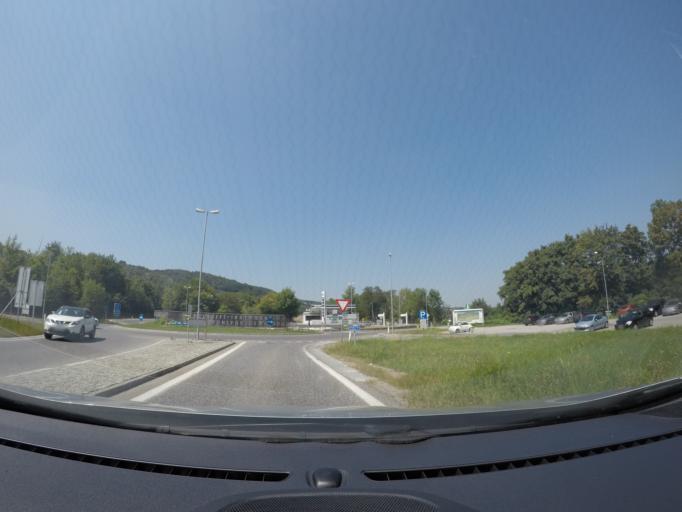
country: AT
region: Lower Austria
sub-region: Politischer Bezirk Sankt Polten
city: Altlengbach
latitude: 48.1545
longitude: 15.9048
